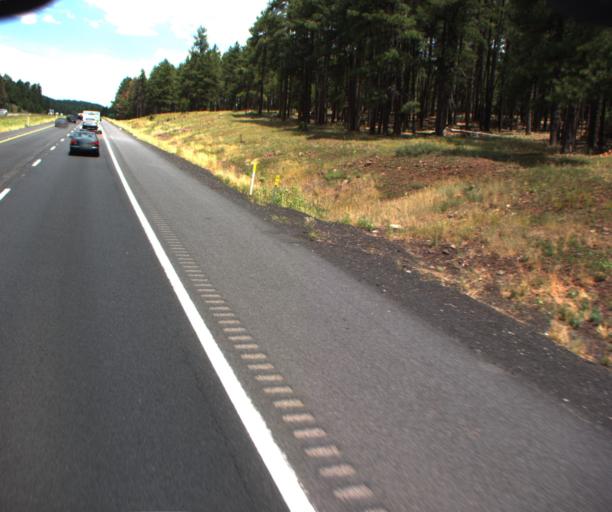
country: US
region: Arizona
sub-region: Coconino County
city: Sedona
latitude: 34.9604
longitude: -111.6794
